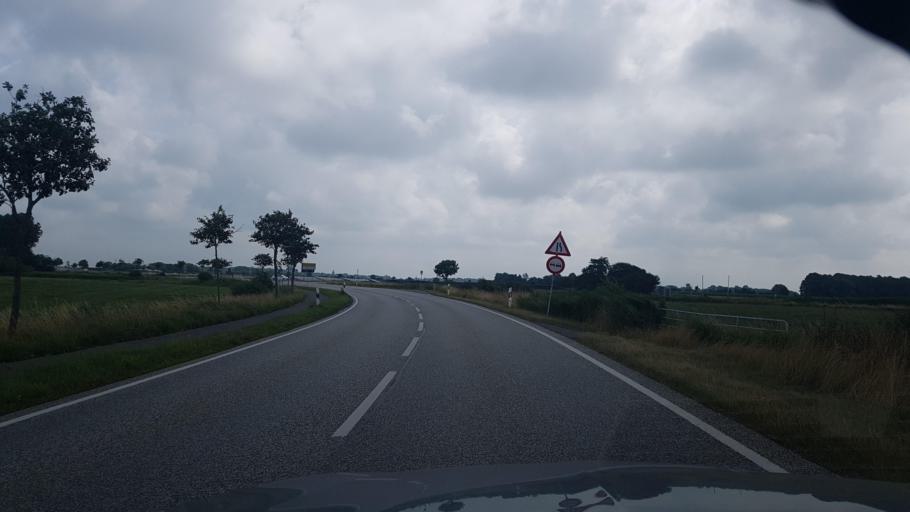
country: DE
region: Schleswig-Holstein
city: Tating
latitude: 54.3248
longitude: 8.7286
